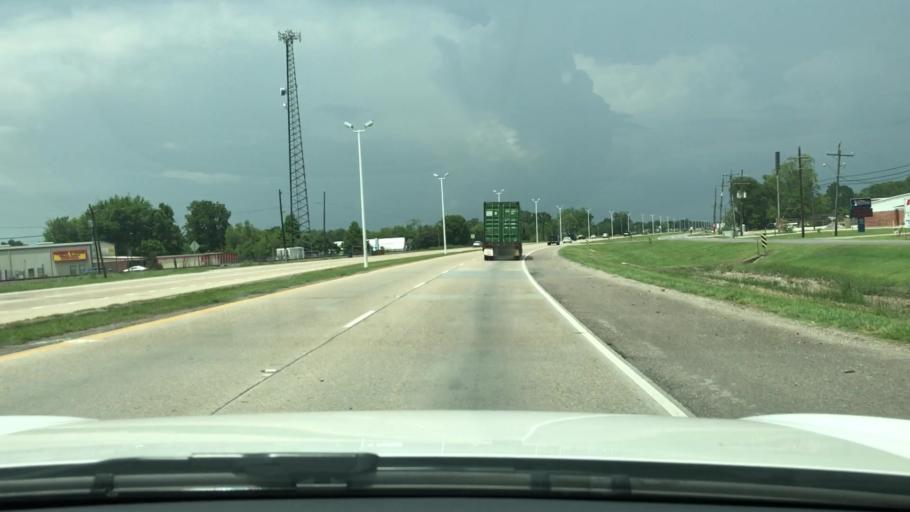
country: US
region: Louisiana
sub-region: West Baton Rouge Parish
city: Addis
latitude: 30.3646
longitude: -91.2605
